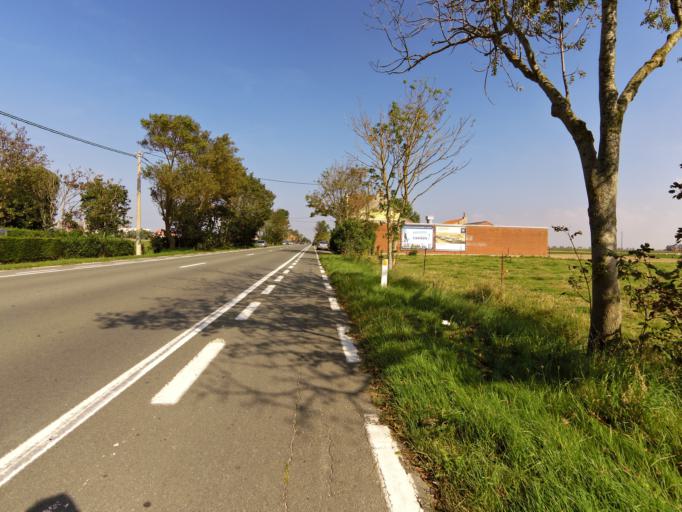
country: BE
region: Flanders
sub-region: Provincie West-Vlaanderen
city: Nieuwpoort
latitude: 51.1628
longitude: 2.7750
